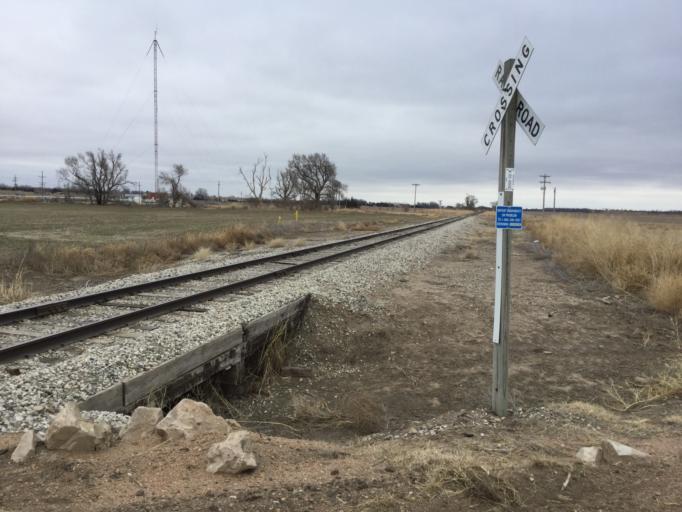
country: US
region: Kansas
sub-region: Barton County
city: Ellinwood
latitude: 38.2899
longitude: -98.4431
